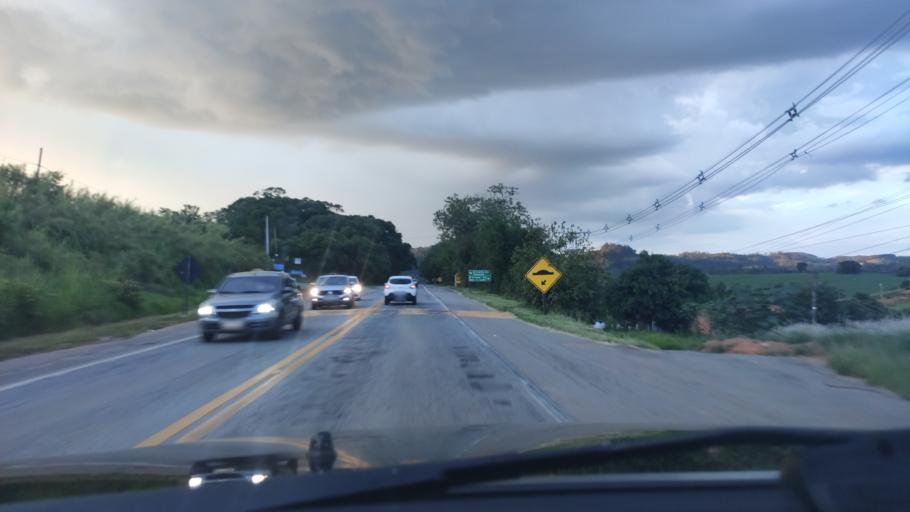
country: BR
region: Sao Paulo
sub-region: Braganca Paulista
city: Braganca Paulista
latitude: -22.8501
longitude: -46.5450
